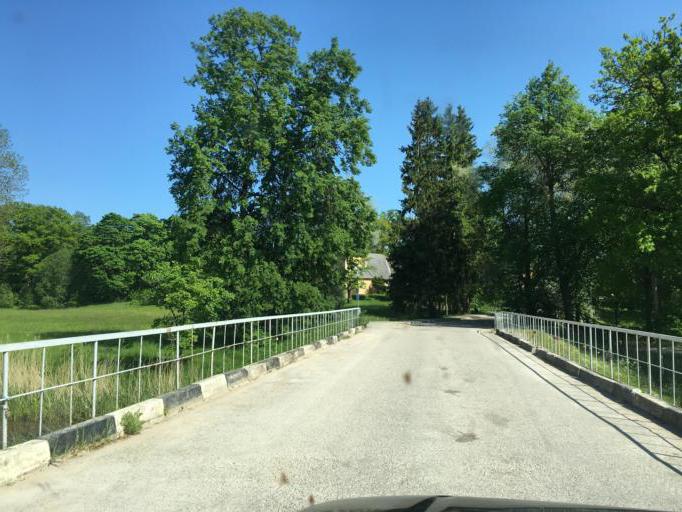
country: LV
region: Dundaga
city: Dundaga
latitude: 57.5104
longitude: 22.3572
